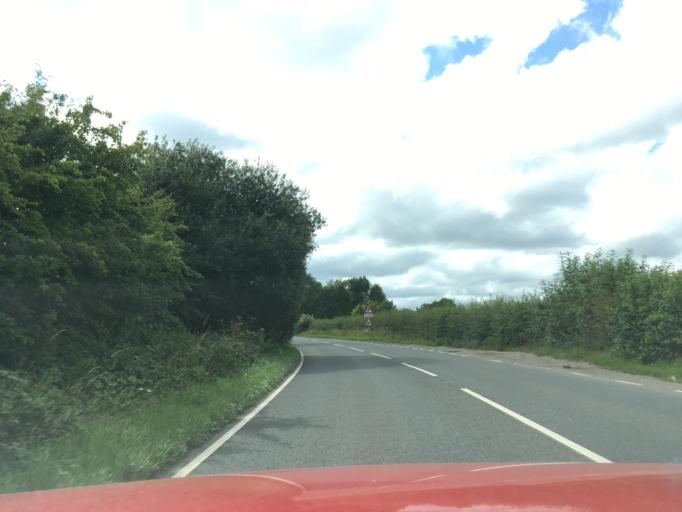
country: GB
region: England
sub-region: West Sussex
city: East Grinstead
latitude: 51.1368
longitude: 0.0280
